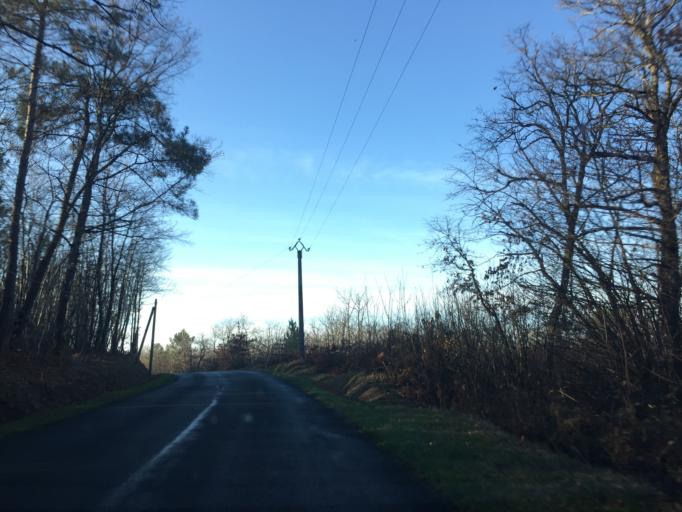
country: FR
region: Aquitaine
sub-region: Departement de la Dordogne
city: Riberac
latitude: 45.2102
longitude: 0.3049
